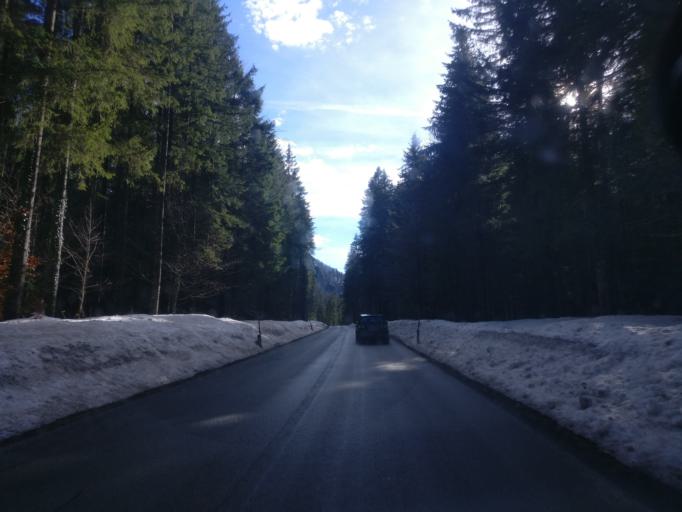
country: AT
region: Styria
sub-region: Politischer Bezirk Liezen
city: Sankt Gallen
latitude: 47.6193
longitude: 14.5431
